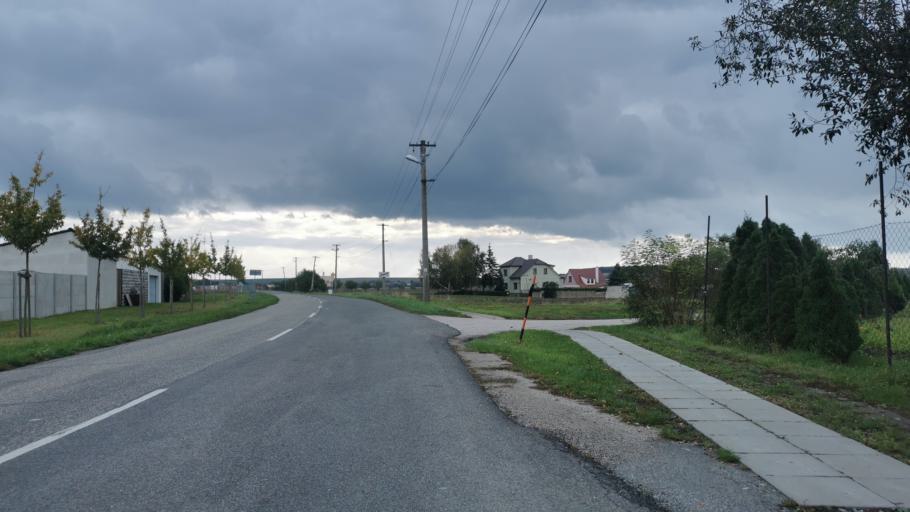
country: SK
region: Trnavsky
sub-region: Okres Skalica
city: Holic
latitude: 48.8181
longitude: 17.1941
